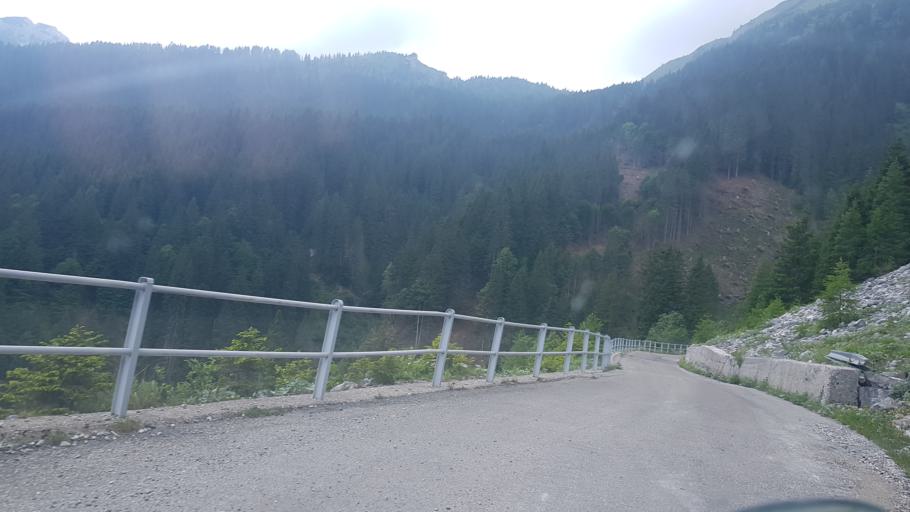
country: IT
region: Friuli Venezia Giulia
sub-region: Provincia di Udine
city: Paularo
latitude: 46.5521
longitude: 13.1924
